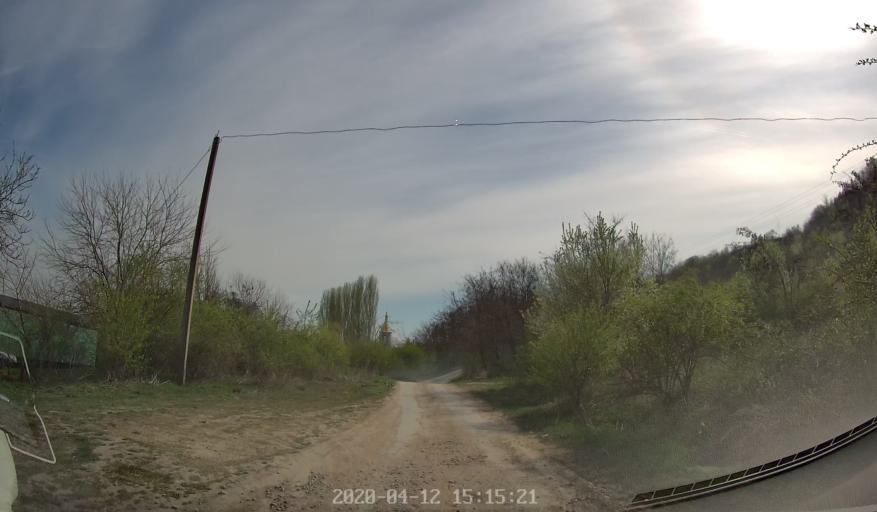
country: MD
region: Telenesti
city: Cocieri
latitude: 47.3222
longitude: 29.0748
